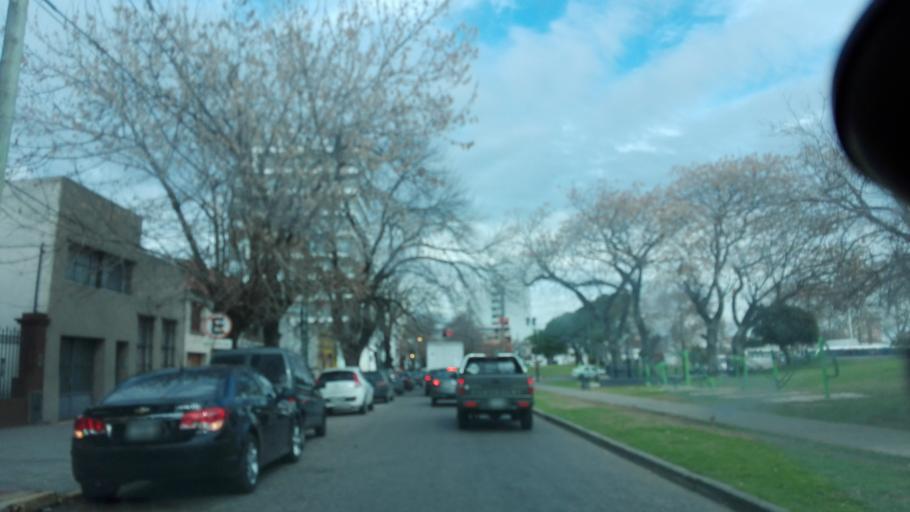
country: AR
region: Buenos Aires
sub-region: Partido de La Plata
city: La Plata
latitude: -34.9123
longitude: -57.9654
